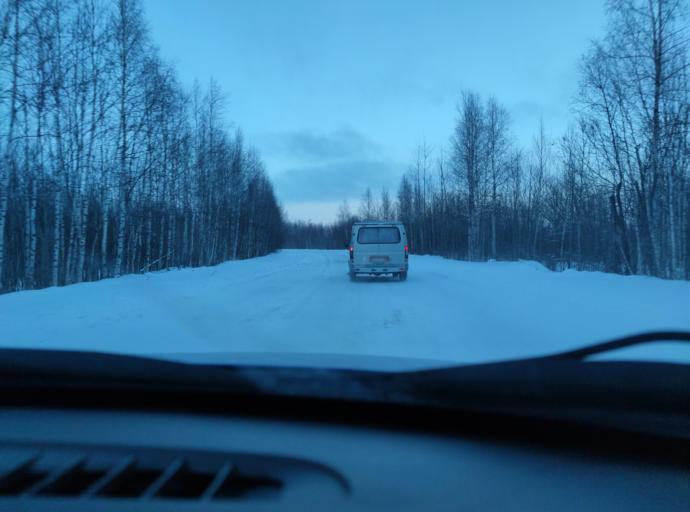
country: RU
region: Khanty-Mansiyskiy Avtonomnyy Okrug
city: Langepas
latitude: 61.1810
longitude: 75.1647
